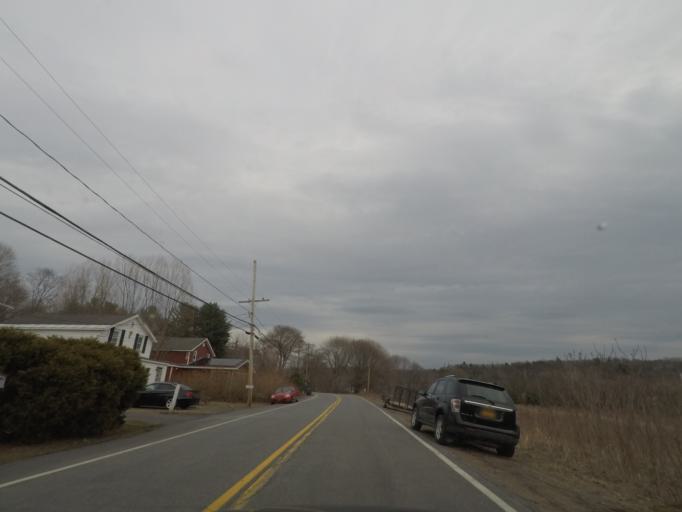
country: US
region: New York
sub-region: Saratoga County
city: Schuylerville
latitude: 43.1174
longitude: -73.5720
